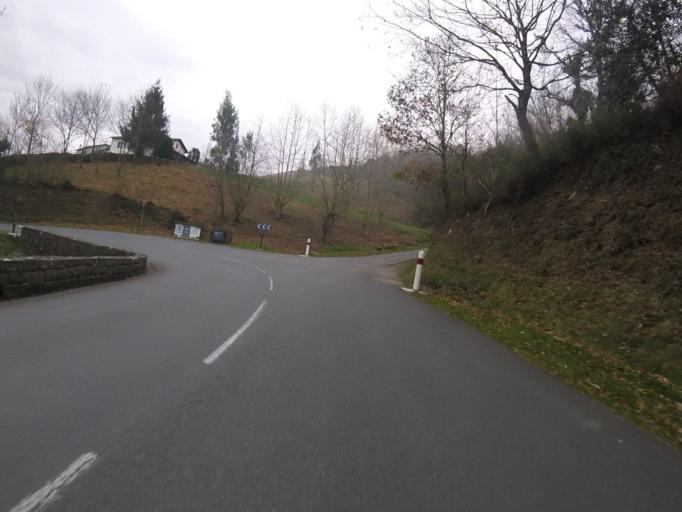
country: FR
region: Aquitaine
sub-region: Departement des Pyrenees-Atlantiques
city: Sare
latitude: 43.3221
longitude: -1.5996
